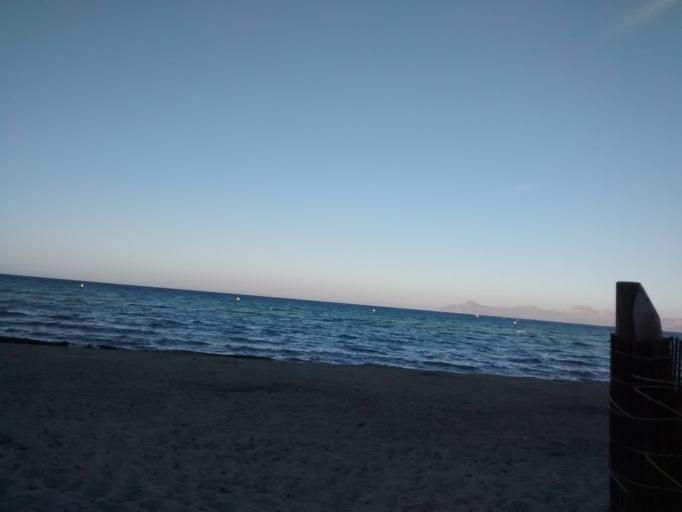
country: ES
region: Balearic Islands
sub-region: Illes Balears
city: Port d'Alcudia
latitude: 39.8104
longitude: 3.1176
